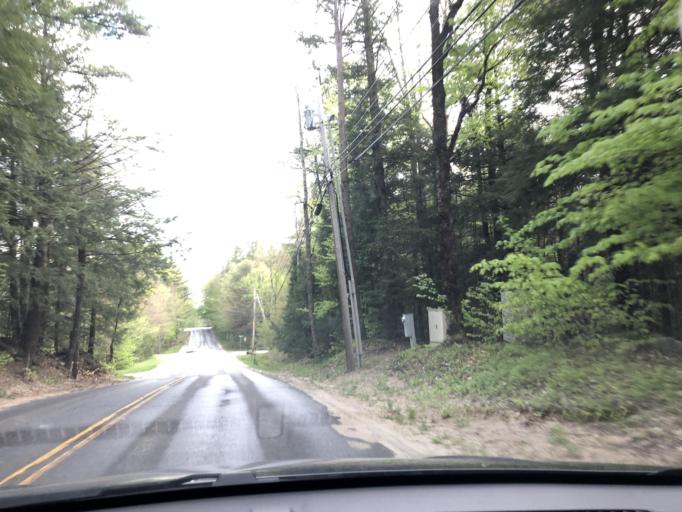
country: US
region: New Hampshire
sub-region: Merrimack County
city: New London
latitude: 43.4169
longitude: -72.0050
